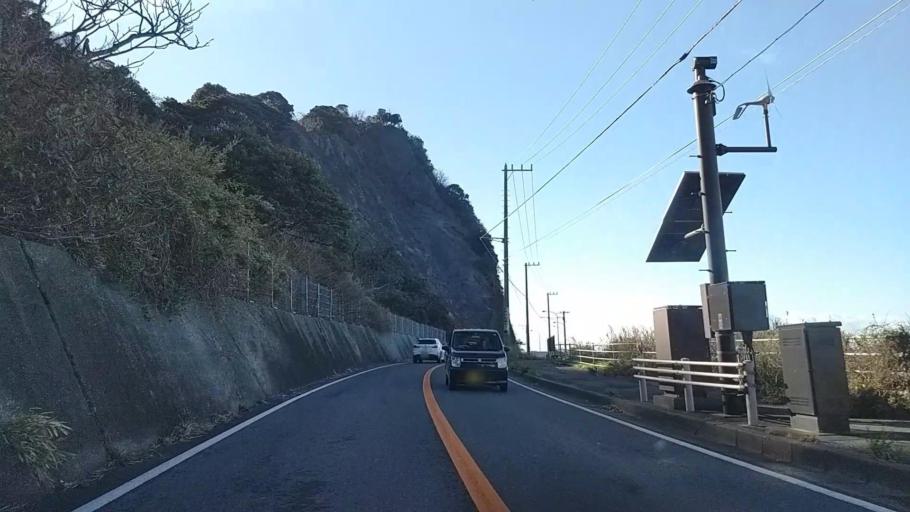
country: JP
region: Chiba
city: Futtsu
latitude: 35.1592
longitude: 139.8198
